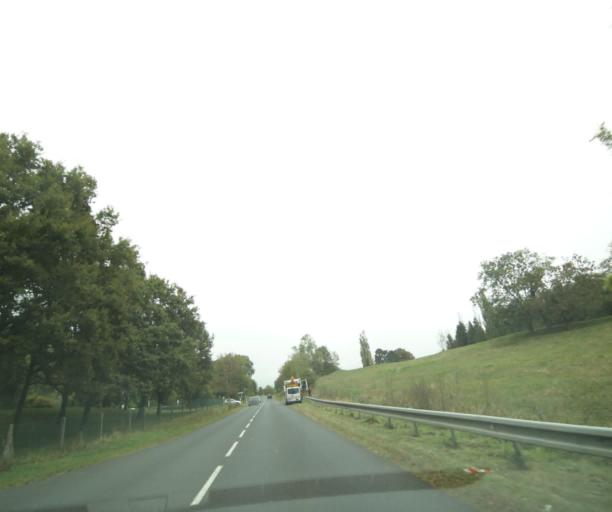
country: FR
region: Auvergne
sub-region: Departement du Puy-de-Dome
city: Saint-Genes-Champanelle
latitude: 45.7113
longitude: 3.0162
